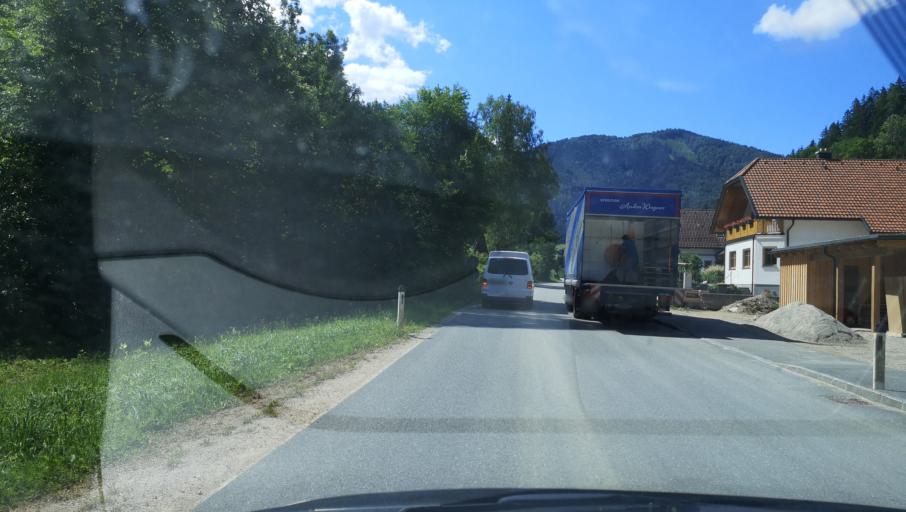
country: AT
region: Lower Austria
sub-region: Politischer Bezirk Scheibbs
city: Gresten
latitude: 47.9404
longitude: 15.0278
